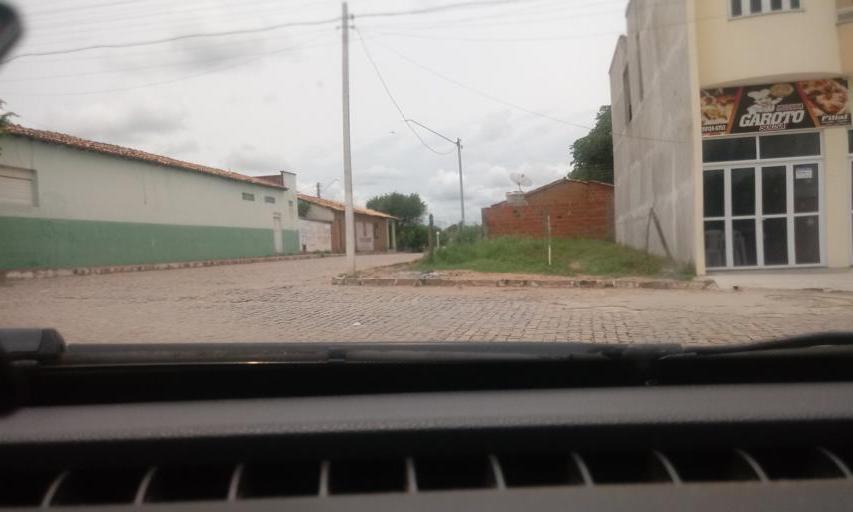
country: BR
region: Bahia
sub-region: Riacho De Santana
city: Riacho de Santana
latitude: -13.9101
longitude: -42.8471
